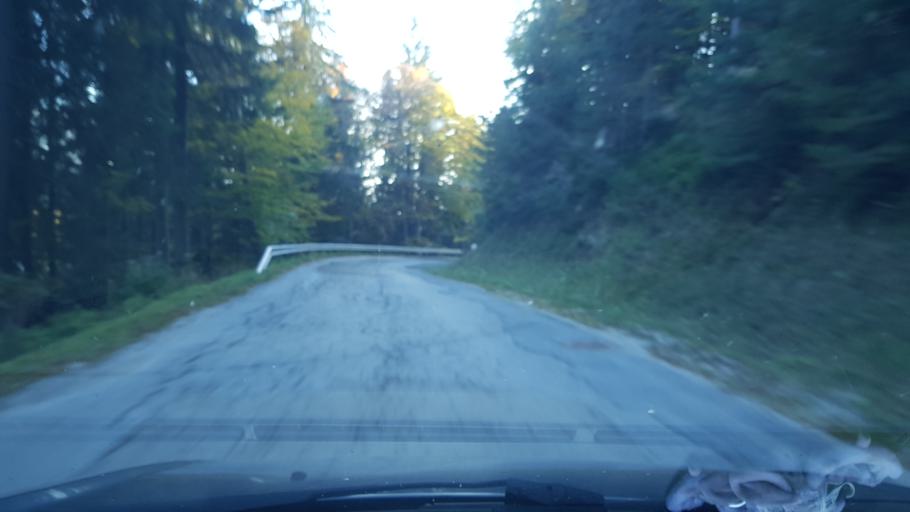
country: SI
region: Slovenj Gradec
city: Legen
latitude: 46.4975
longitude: 15.1925
